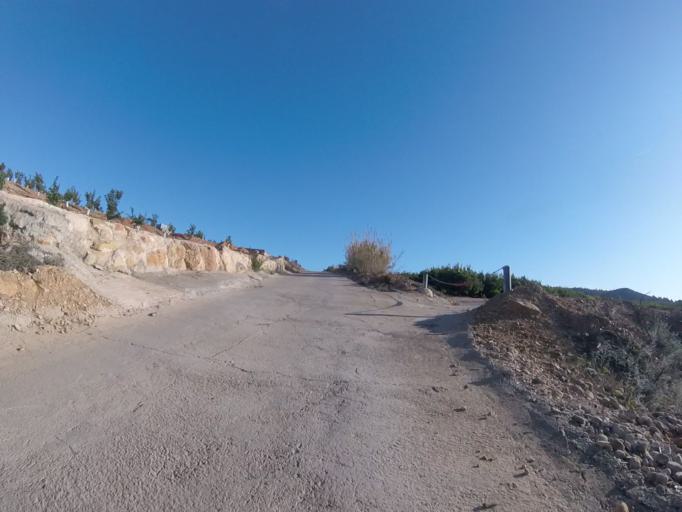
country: ES
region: Valencia
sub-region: Provincia de Castello
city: Alcala de Xivert
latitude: 40.2658
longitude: 0.2049
